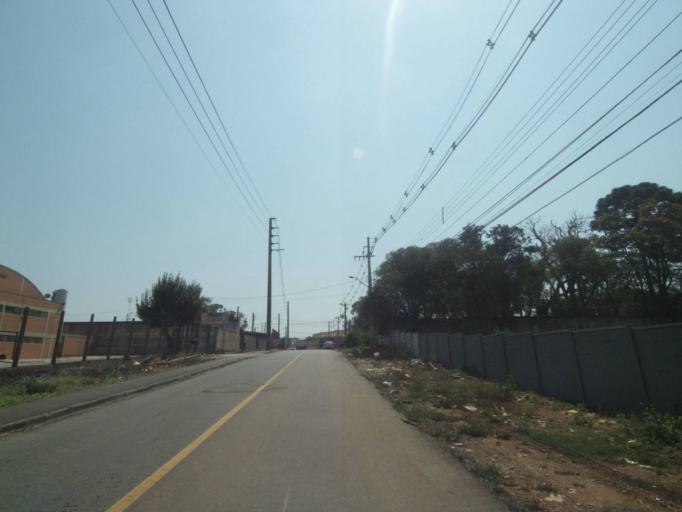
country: BR
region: Parana
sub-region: Sao Jose Dos Pinhais
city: Sao Jose dos Pinhais
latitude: -25.4977
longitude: -49.2702
